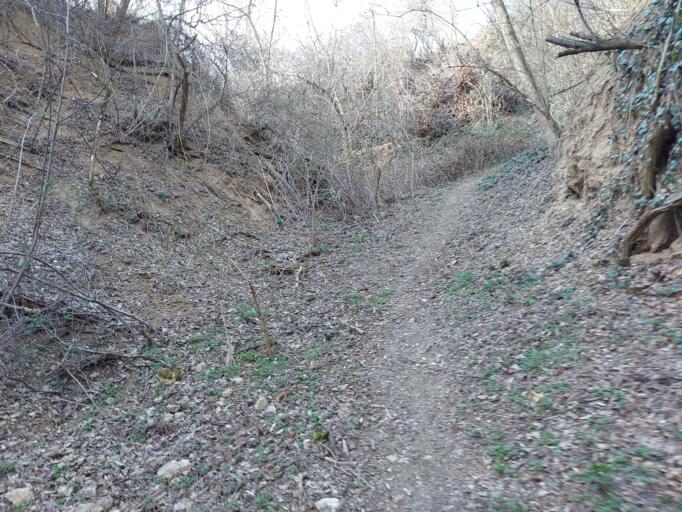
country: HU
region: Pest
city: Budaors
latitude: 47.4743
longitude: 18.9637
